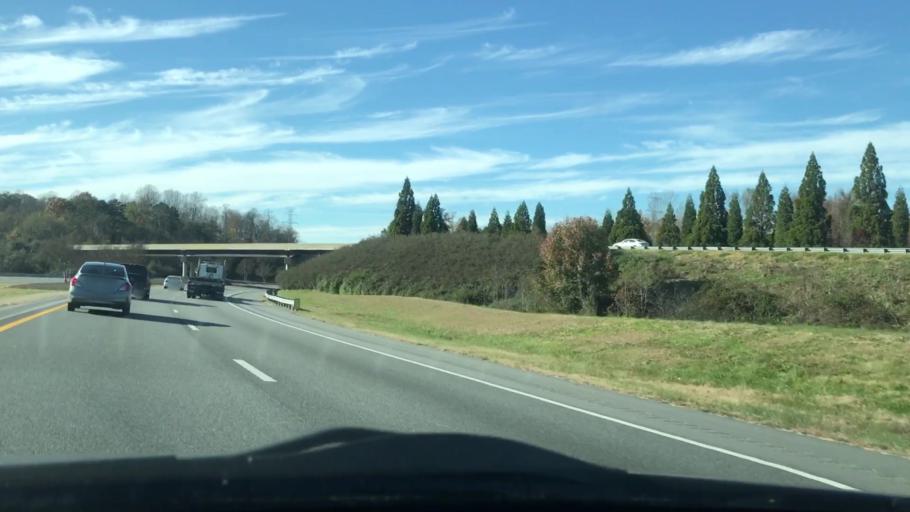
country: US
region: North Carolina
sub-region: Guilford County
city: High Point
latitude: 36.0072
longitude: -80.0296
